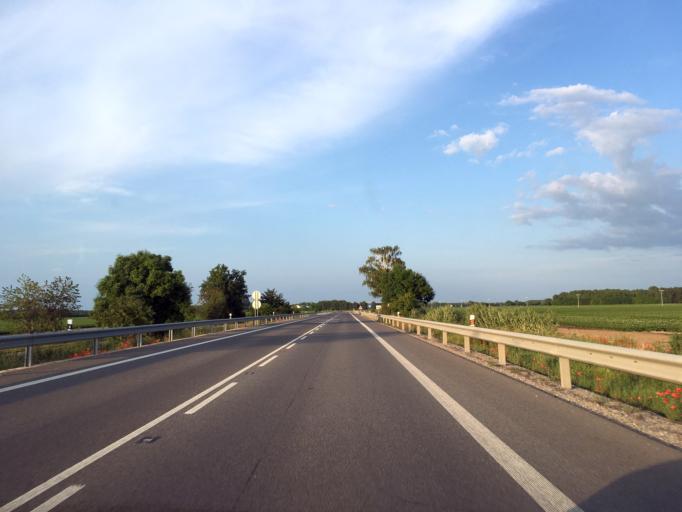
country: SK
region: Trnavsky
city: Sladkovicovo
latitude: 48.2020
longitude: 17.5404
